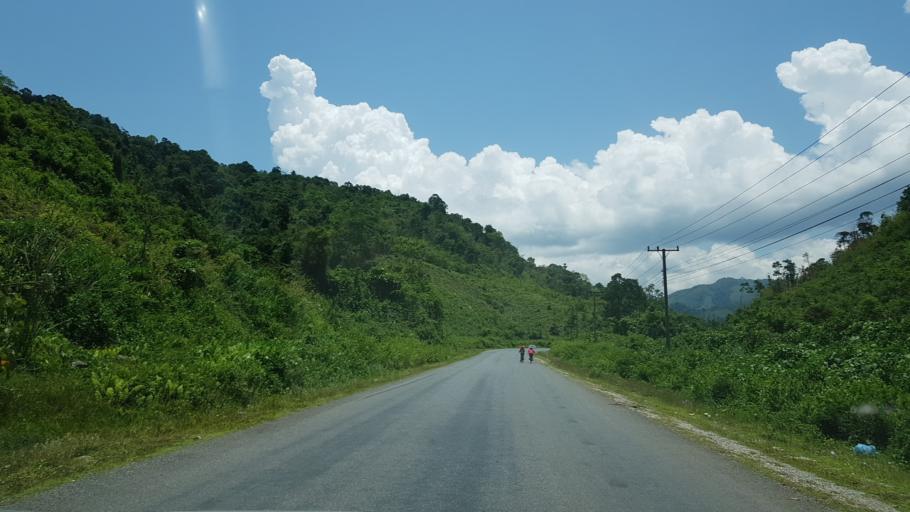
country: LA
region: Vientiane
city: Muang Kasi
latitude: 19.1315
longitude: 102.2333
